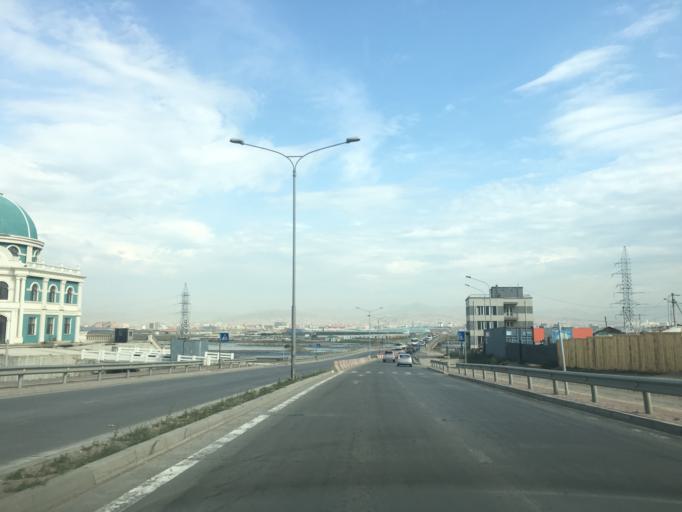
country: MN
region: Ulaanbaatar
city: Ulaanbaatar
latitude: 47.8708
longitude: 106.7846
